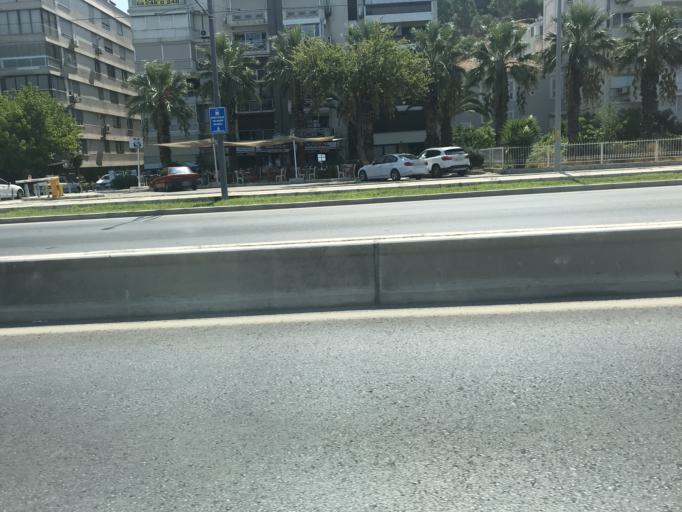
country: TR
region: Izmir
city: Izmir
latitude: 38.4009
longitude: 27.0920
